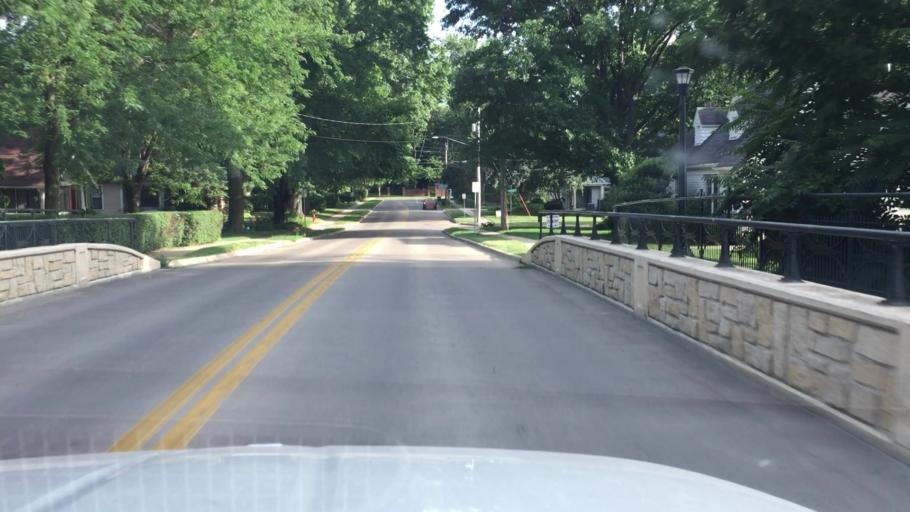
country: US
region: Iowa
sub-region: Johnson County
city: Iowa City
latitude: 41.6512
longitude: -91.5211
